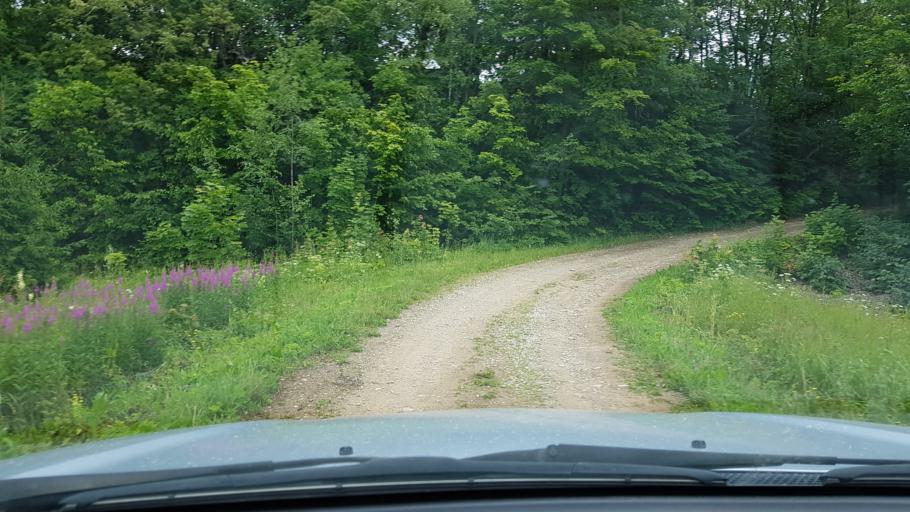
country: EE
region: Ida-Virumaa
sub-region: Narva-Joesuu linn
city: Narva-Joesuu
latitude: 59.4021
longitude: 27.9739
